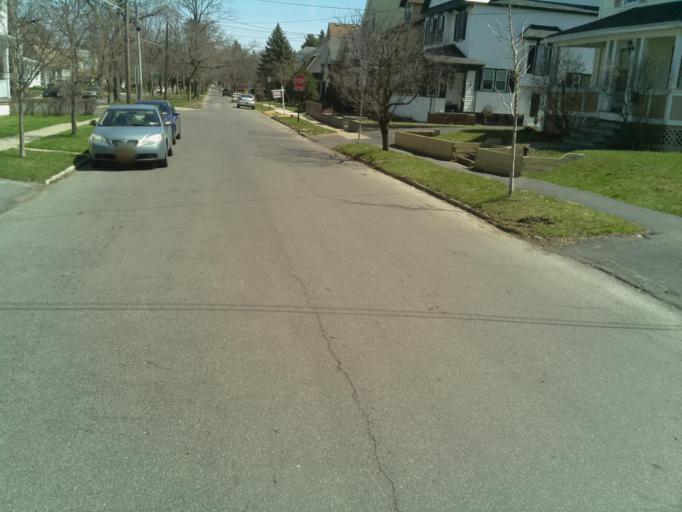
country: US
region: New York
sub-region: Onondaga County
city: Lyncourt
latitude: 43.0642
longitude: -76.1192
